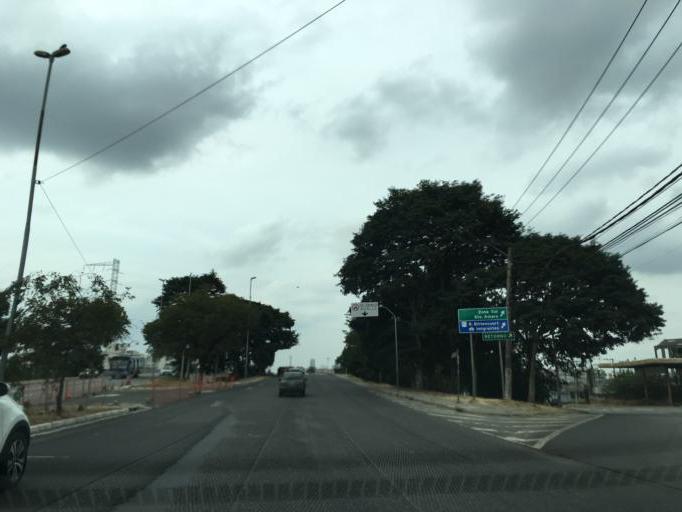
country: BR
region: Sao Paulo
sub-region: Osasco
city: Osasco
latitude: -23.5476
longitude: -46.7365
